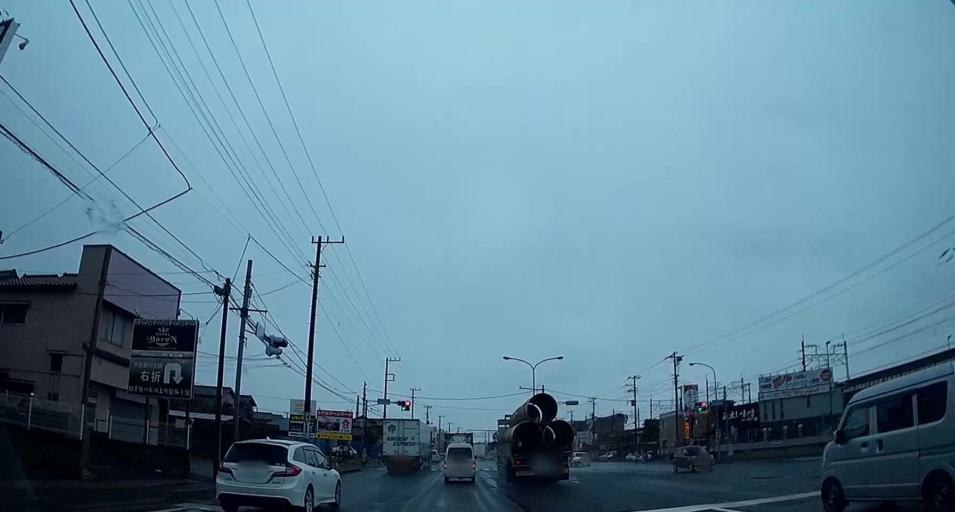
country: JP
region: Chiba
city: Chiba
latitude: 35.5941
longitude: 140.1204
